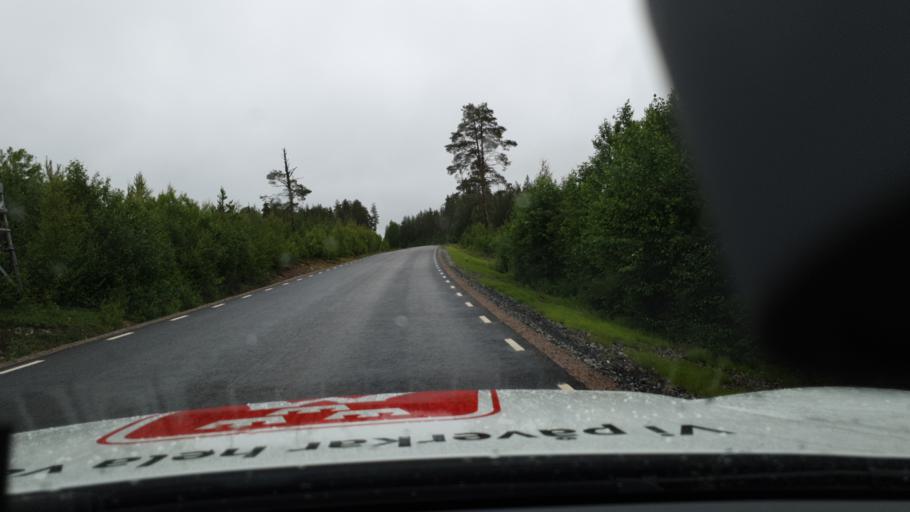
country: SE
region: Norrbotten
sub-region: Overtornea Kommun
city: OEvertornea
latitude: 66.5674
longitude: 23.3325
